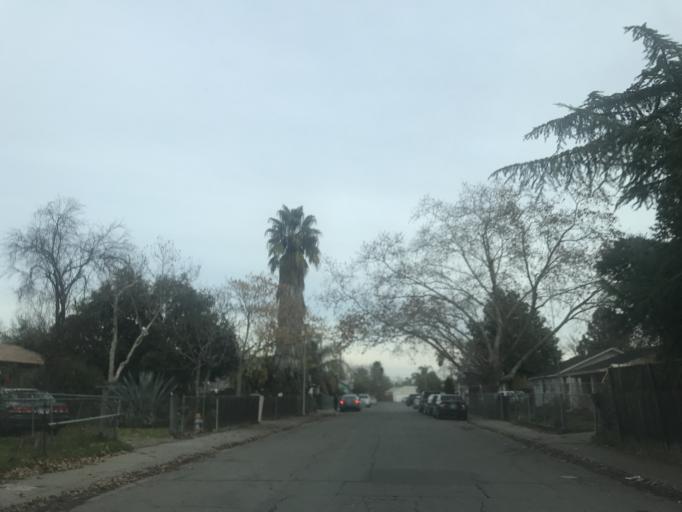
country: US
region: California
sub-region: Sacramento County
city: Parkway
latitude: 38.5290
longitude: -121.4666
